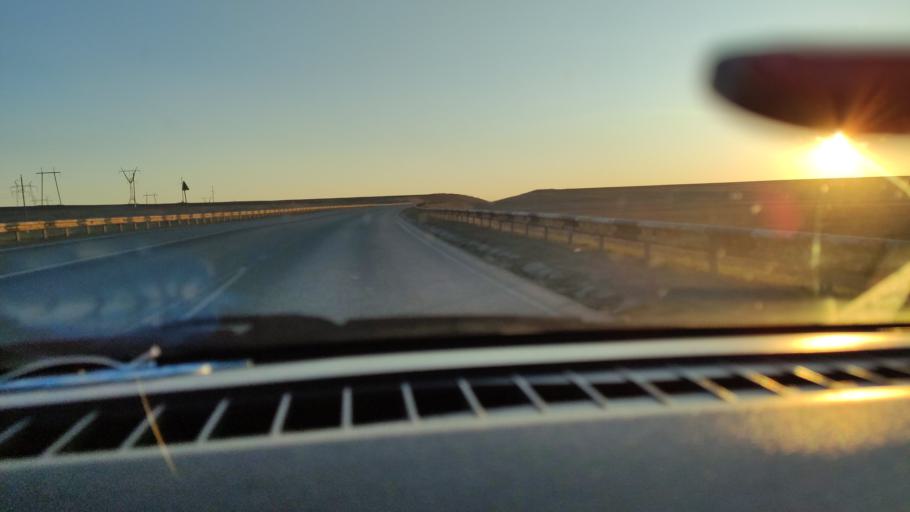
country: RU
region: Saratov
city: Sinodskoye
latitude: 51.9250
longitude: 46.5650
